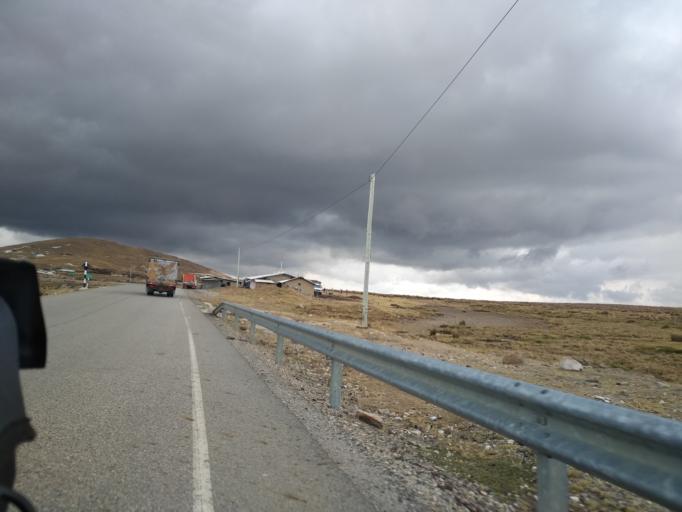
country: PE
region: La Libertad
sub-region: Provincia de Santiago de Chuco
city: Quiruvilca
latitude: -7.9903
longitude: -78.2897
